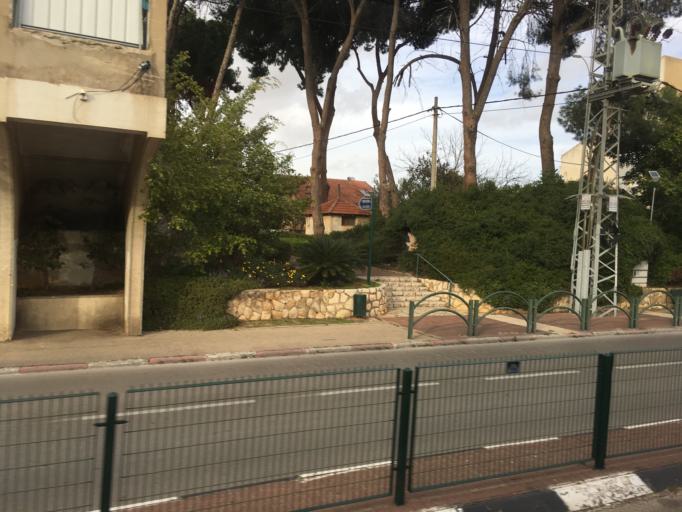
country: IL
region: Central District
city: Kfar Saba
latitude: 32.1781
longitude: 34.8966
